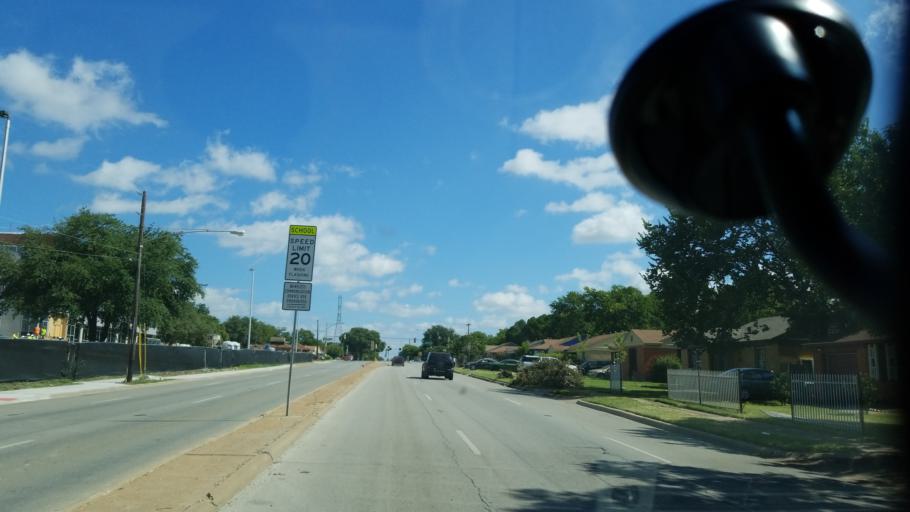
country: US
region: Texas
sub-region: Dallas County
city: Cockrell Hill
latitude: 32.6990
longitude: -96.8147
